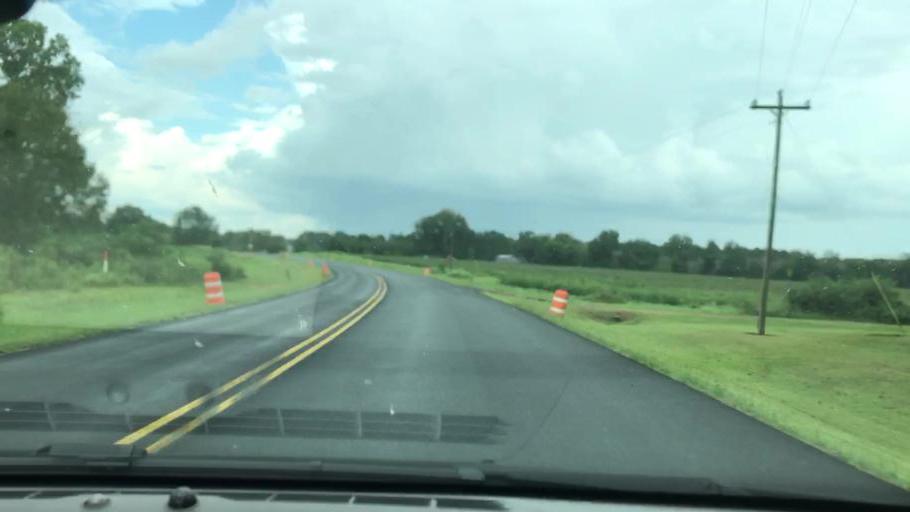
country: US
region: Georgia
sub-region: Early County
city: Blakely
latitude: 31.4198
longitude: -84.9632
